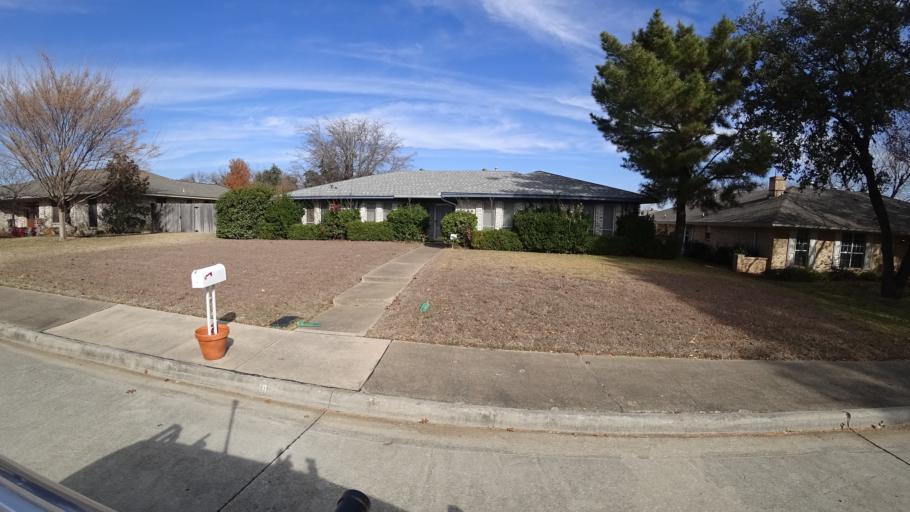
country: US
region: Texas
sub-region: Denton County
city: Lewisville
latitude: 33.0500
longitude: -97.0306
